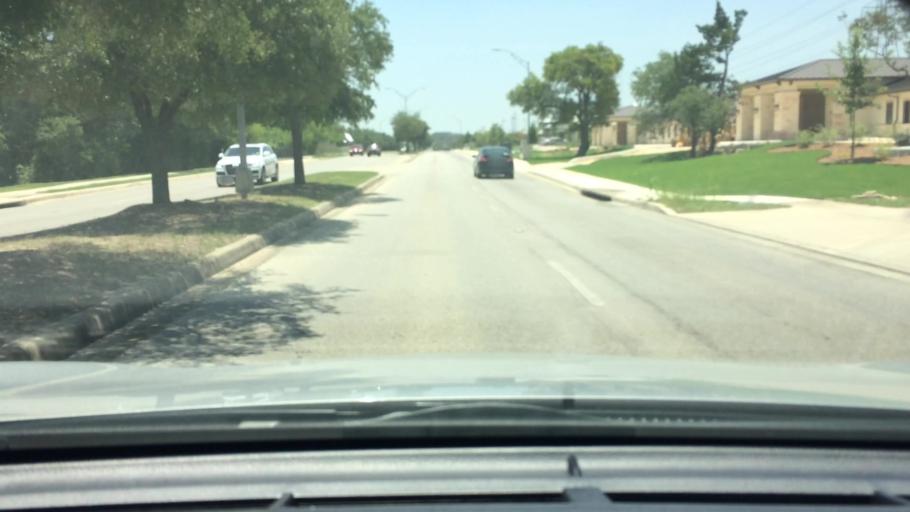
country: US
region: Texas
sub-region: Bexar County
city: Shavano Park
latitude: 29.5848
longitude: -98.5709
